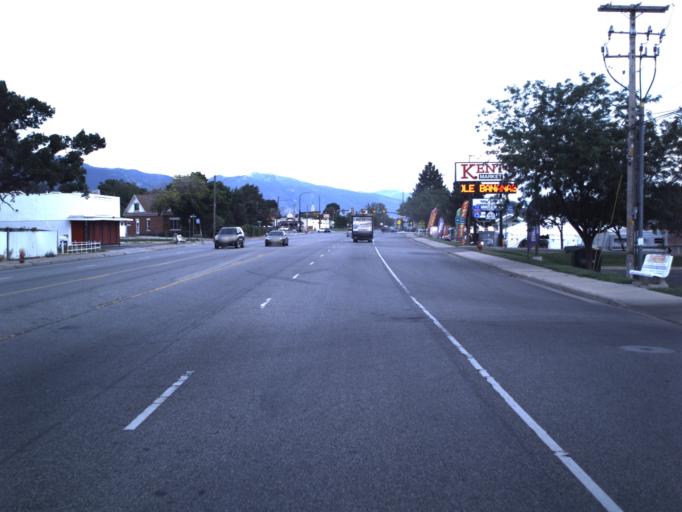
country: US
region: Utah
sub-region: Davis County
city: Clearfield
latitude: 41.1056
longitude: -112.0177
